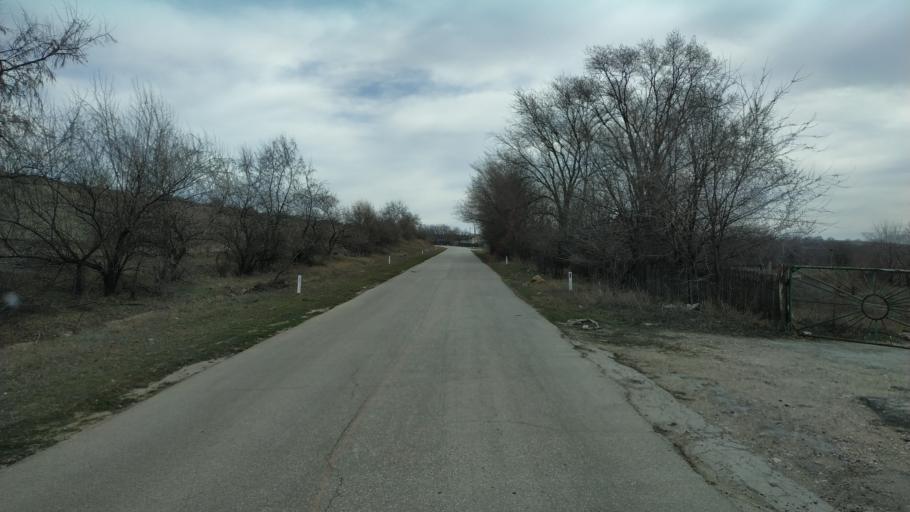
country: MD
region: Nisporeni
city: Nisporeni
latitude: 46.9553
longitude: 28.2231
